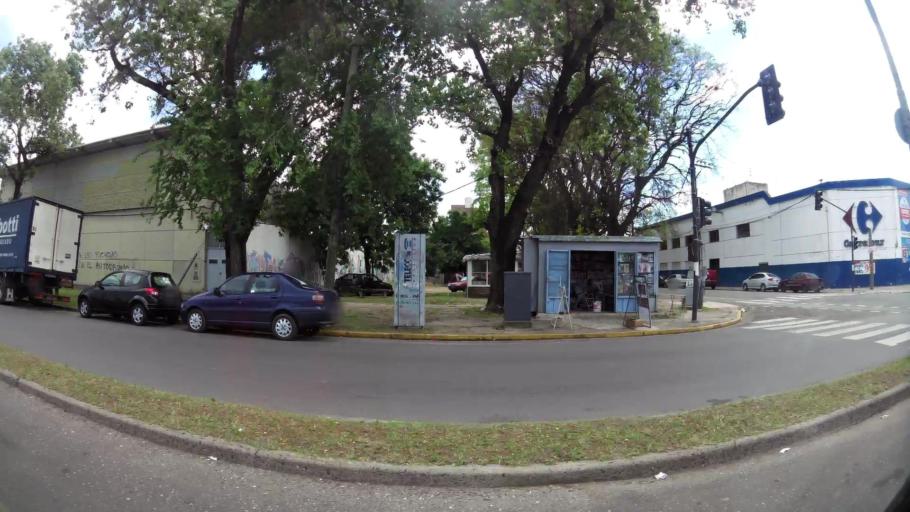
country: AR
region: Santa Fe
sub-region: Departamento de Rosario
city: Rosario
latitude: -32.9701
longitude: -60.6297
